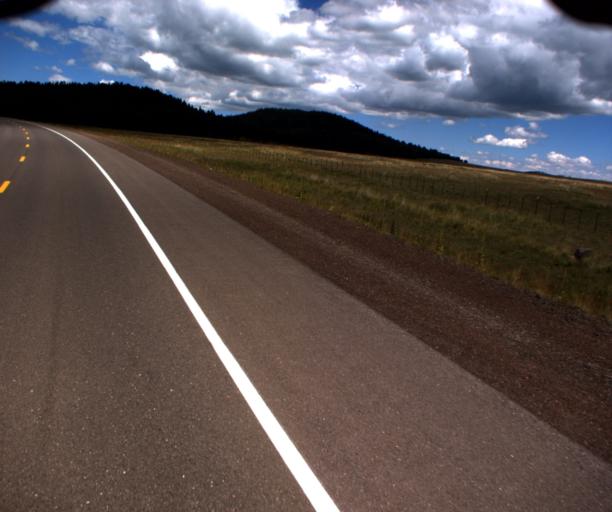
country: US
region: Arizona
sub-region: Apache County
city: Eagar
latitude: 34.0127
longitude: -109.5670
